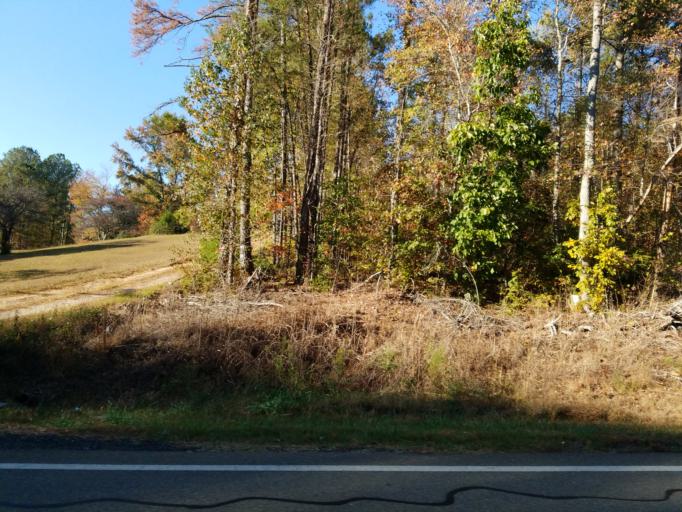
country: US
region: Georgia
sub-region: Pickens County
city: Jasper
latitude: 34.5213
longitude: -84.4868
